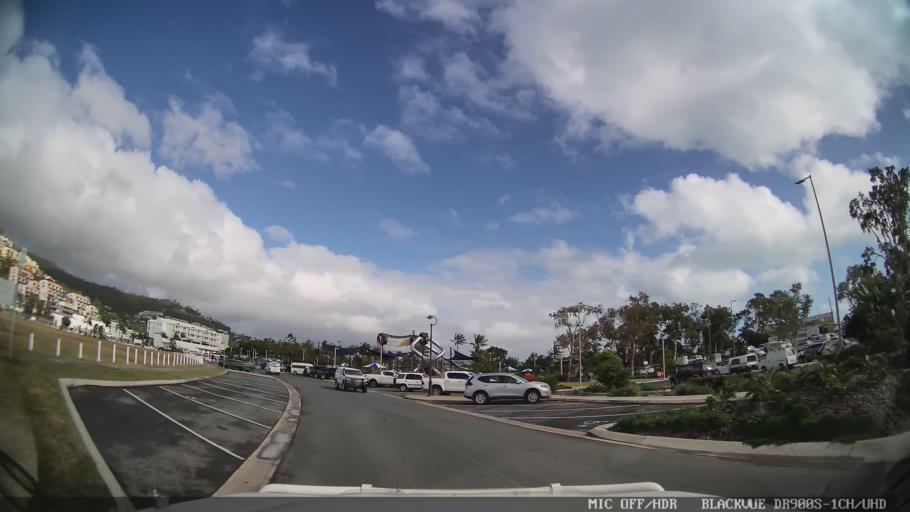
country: AU
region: Queensland
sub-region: Whitsunday
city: Proserpine
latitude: -20.2683
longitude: 148.7232
